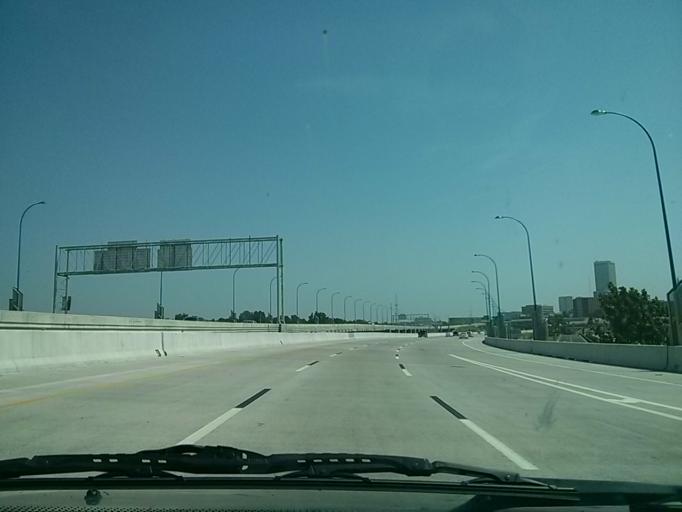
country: US
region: Oklahoma
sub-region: Tulsa County
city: Tulsa
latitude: 36.1406
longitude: -96.0070
